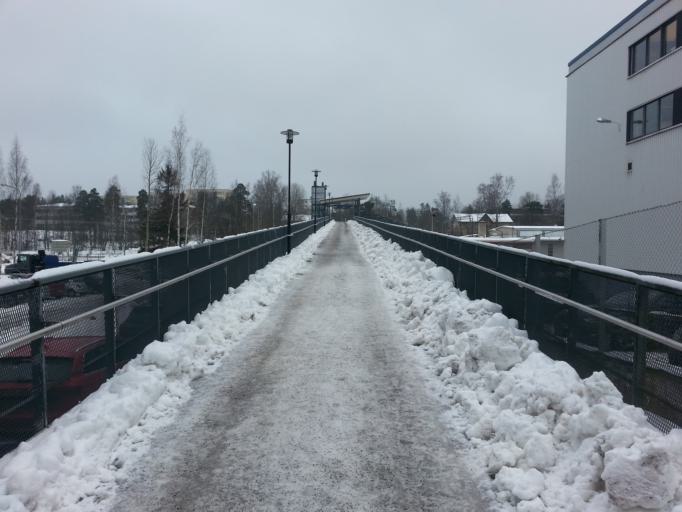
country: FI
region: Uusimaa
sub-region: Helsinki
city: Teekkarikylae
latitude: 60.2225
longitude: 24.8572
